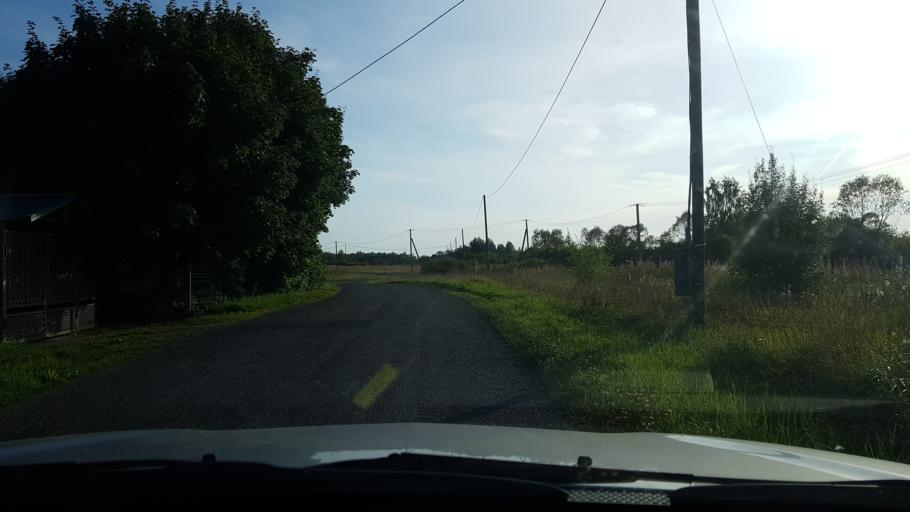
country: EE
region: Ida-Virumaa
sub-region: Narva-Joesuu linn
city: Narva-Joesuu
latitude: 59.3504
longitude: 28.0296
